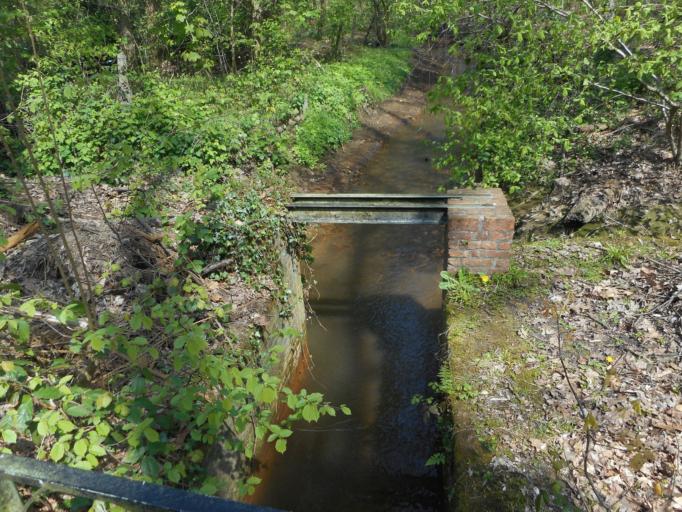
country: BE
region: Flanders
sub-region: Provincie Antwerpen
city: Zoersel
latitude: 51.2652
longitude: 4.6897
